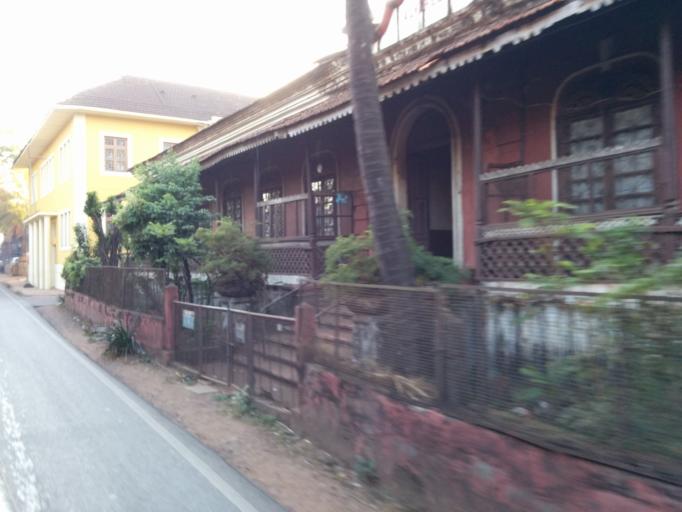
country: IN
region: Goa
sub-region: South Goa
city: Madgaon
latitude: 15.2815
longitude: 73.9574
